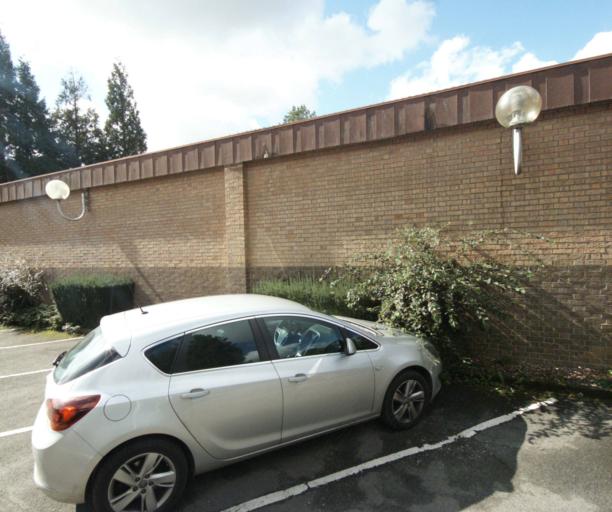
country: FR
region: Nord-Pas-de-Calais
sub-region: Departement du Nord
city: Loos
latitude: 50.6201
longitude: 3.0151
